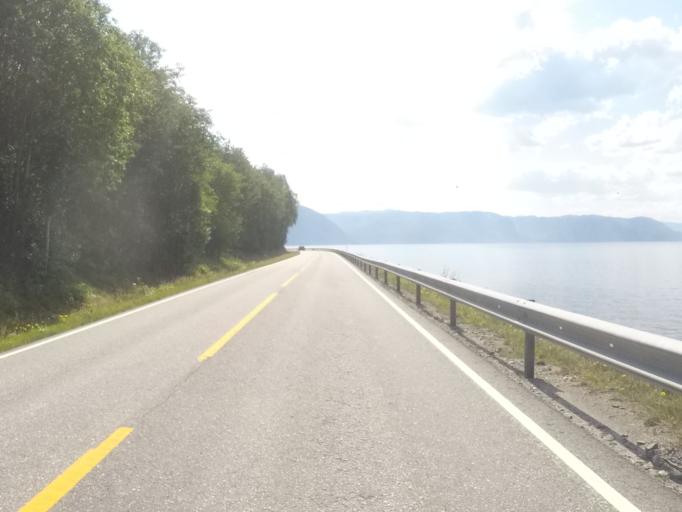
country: NO
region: Sogn og Fjordane
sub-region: Gaular
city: Sande
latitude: 61.1496
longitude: 5.6246
